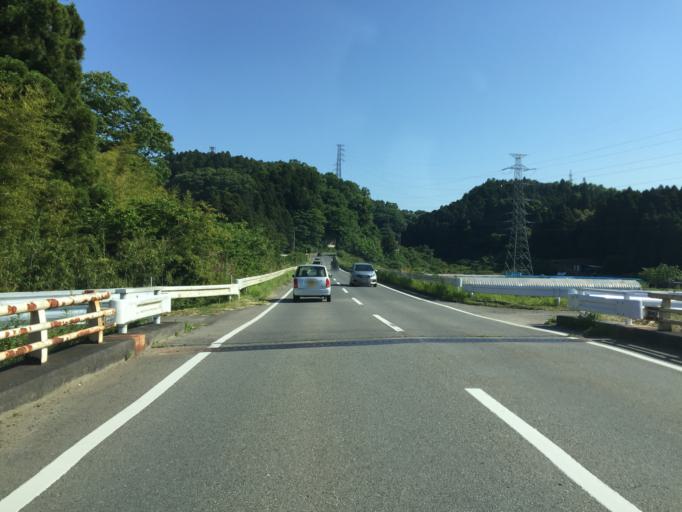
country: JP
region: Fukushima
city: Iwaki
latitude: 36.9551
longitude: 140.8280
